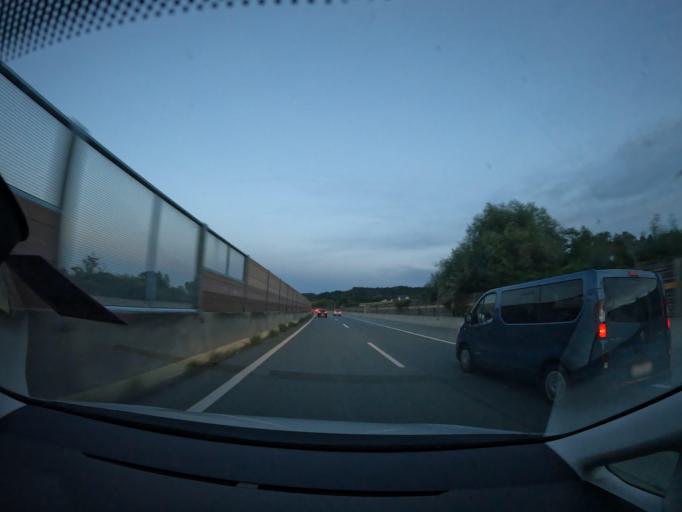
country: AT
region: Styria
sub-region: Politischer Bezirk Hartberg-Fuerstenfeld
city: Nestelbach im Ilztal
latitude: 47.0845
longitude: 15.8861
